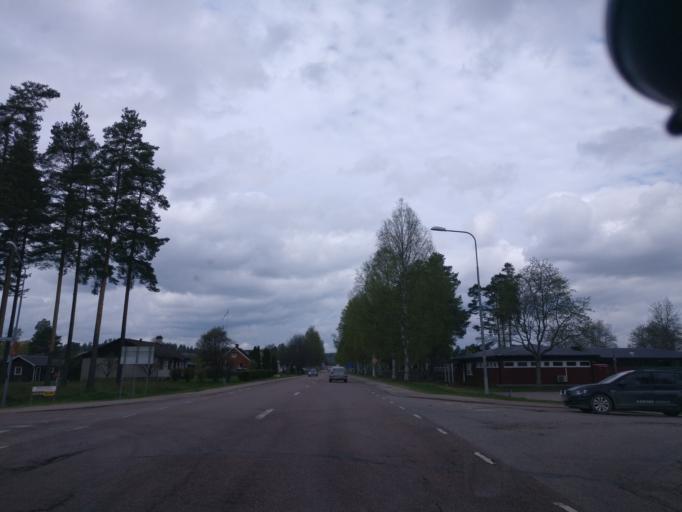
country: SE
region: Vaermland
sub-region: Hagfors Kommun
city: Ekshaerad
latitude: 60.1691
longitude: 13.4977
